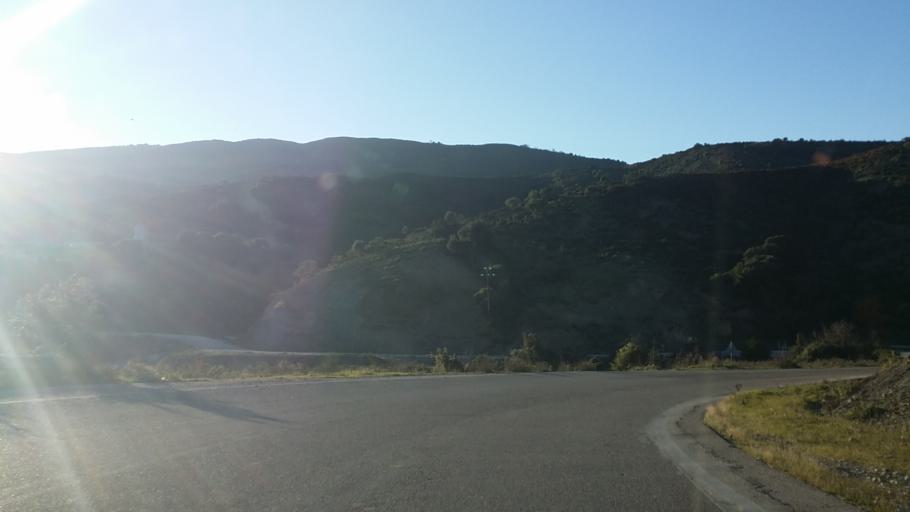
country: GR
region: West Greece
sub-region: Nomos Aitolias kai Akarnanias
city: Lepenou
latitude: 38.8382
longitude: 21.3307
